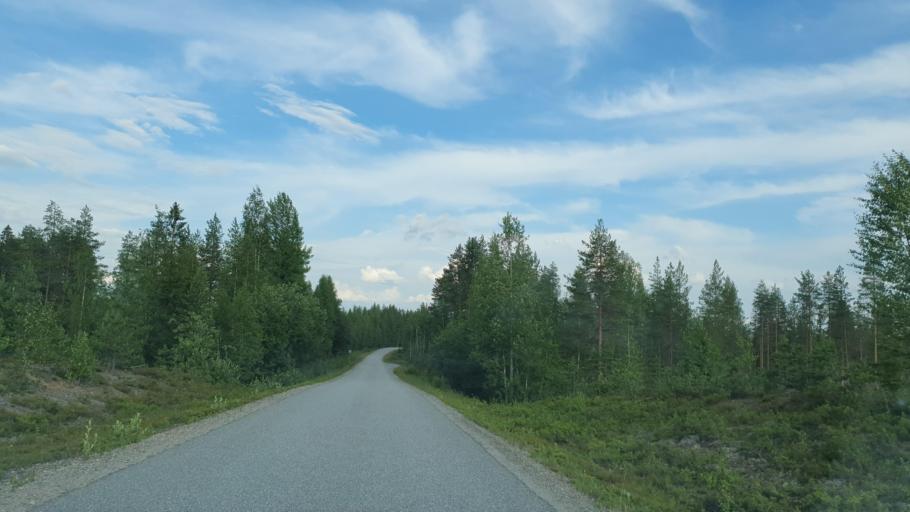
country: FI
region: Kainuu
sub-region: Kehys-Kainuu
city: Kuhmo
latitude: 64.2801
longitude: 29.4187
